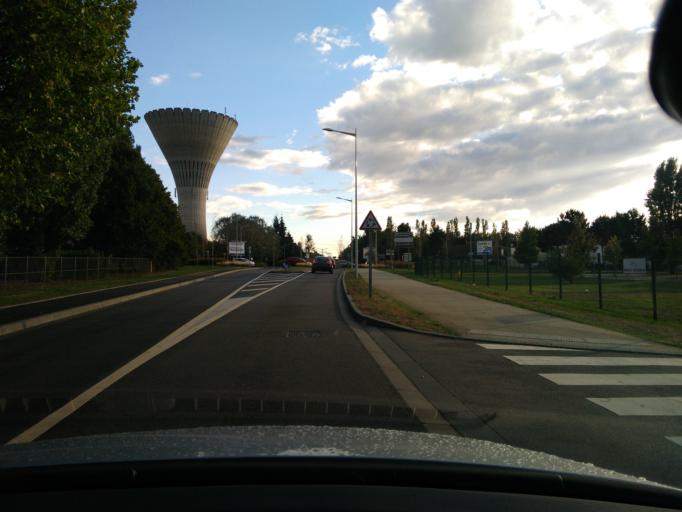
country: FR
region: Haute-Normandie
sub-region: Departement de l'Eure
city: Evreux
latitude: 49.0178
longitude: 1.1714
